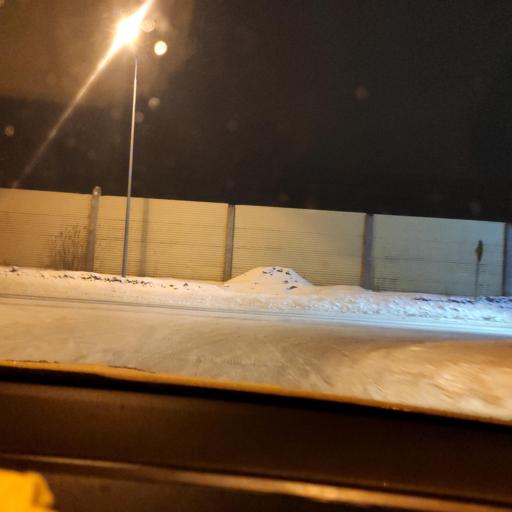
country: RU
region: Moskovskaya
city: Rozhdestveno
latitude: 55.8061
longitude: 36.9984
